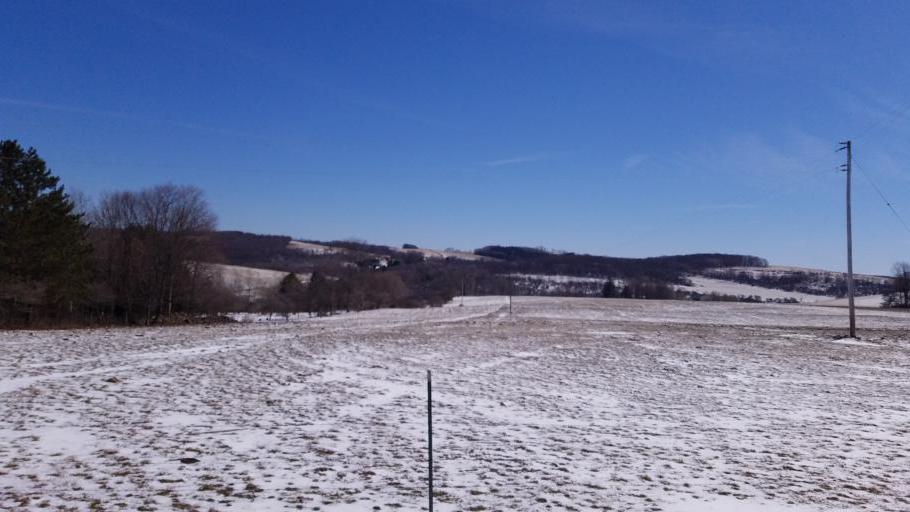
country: US
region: New York
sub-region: Allegany County
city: Andover
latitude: 42.0103
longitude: -77.7726
